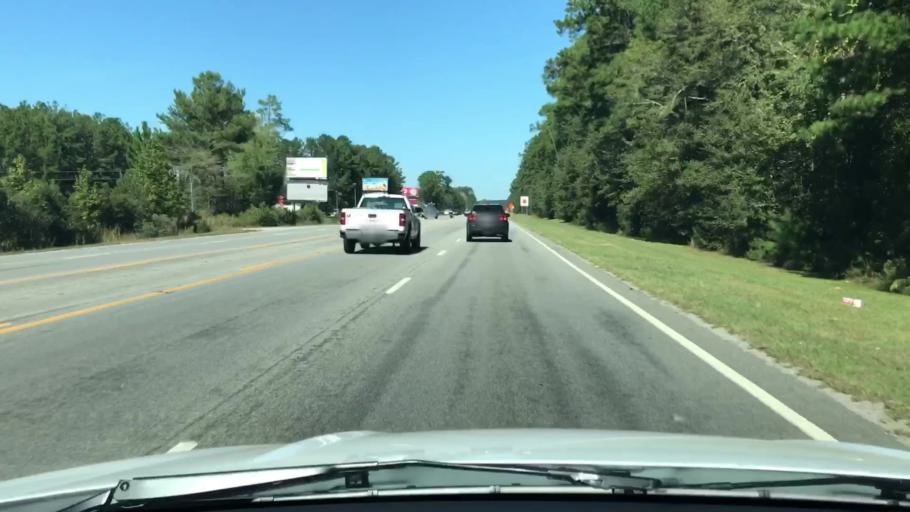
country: US
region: South Carolina
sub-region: Beaufort County
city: Bluffton
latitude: 32.3046
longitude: -80.9351
